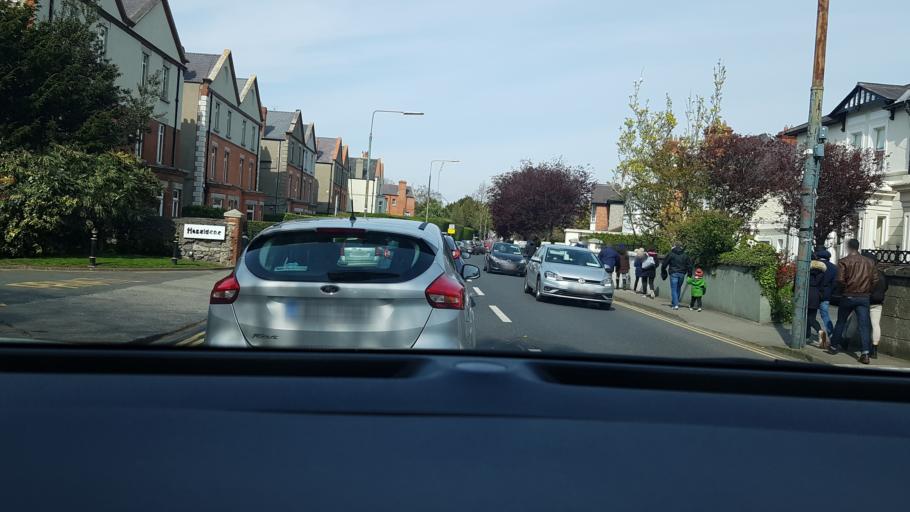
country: IE
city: Clonskeagh
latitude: 53.3231
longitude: -6.2303
